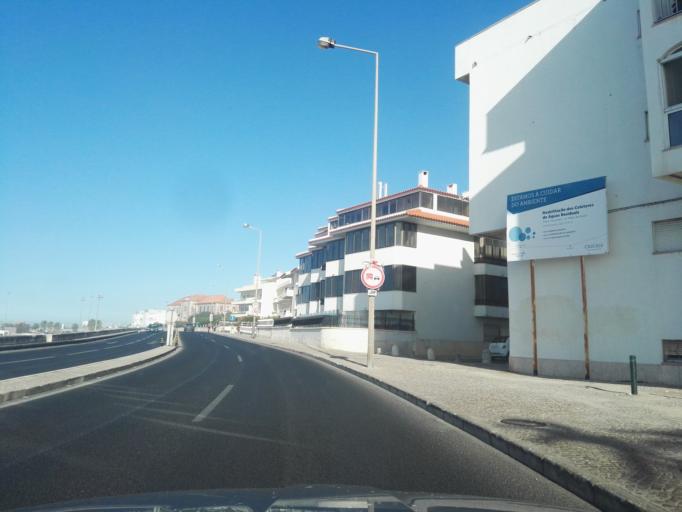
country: PT
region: Lisbon
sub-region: Cascais
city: Parede
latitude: 38.6858
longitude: -9.3529
